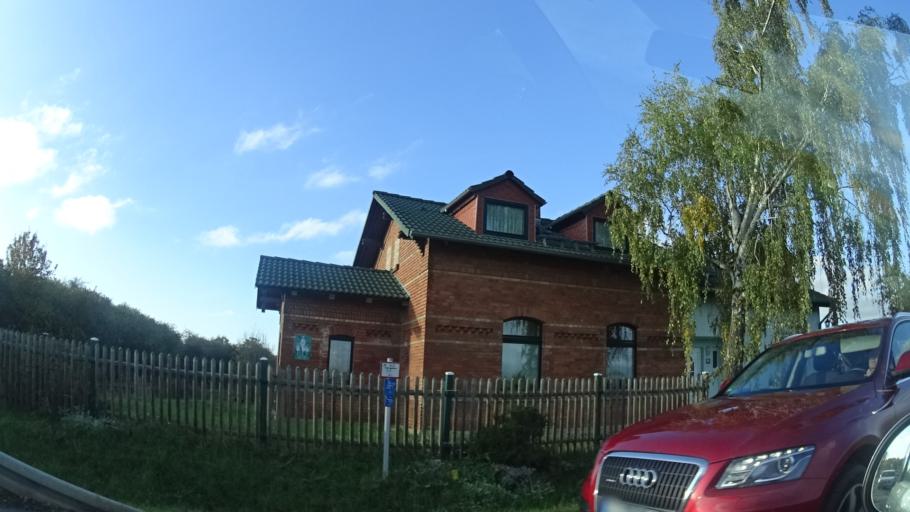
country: DE
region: Thuringia
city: Dornheim
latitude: 50.8294
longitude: 10.9868
